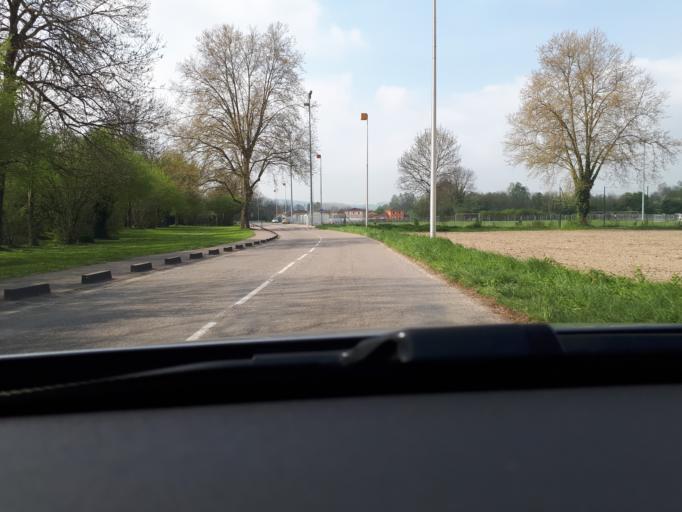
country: FR
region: Rhone-Alpes
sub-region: Departement de l'Isere
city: Bourgoin-Jallieu
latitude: 45.6120
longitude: 5.2642
